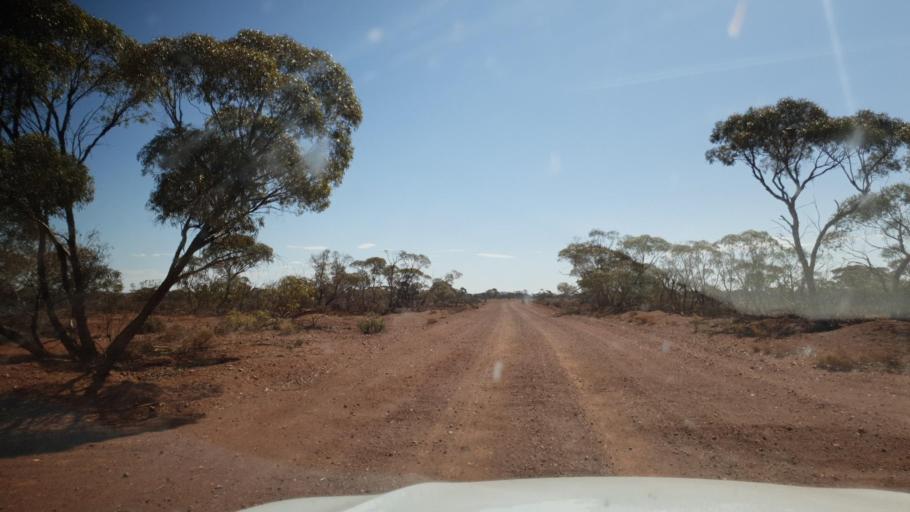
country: AU
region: South Australia
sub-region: Kimba
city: Caralue
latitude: -32.4992
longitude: 136.0883
